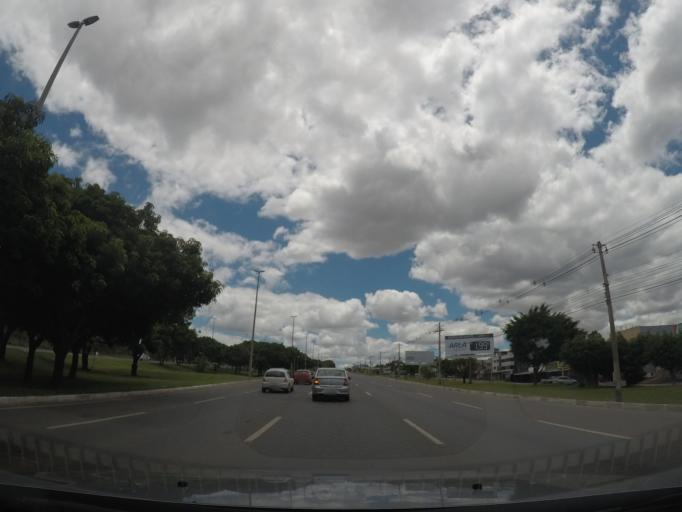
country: BR
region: Federal District
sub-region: Brasilia
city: Brasilia
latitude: -15.7471
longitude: -47.9215
